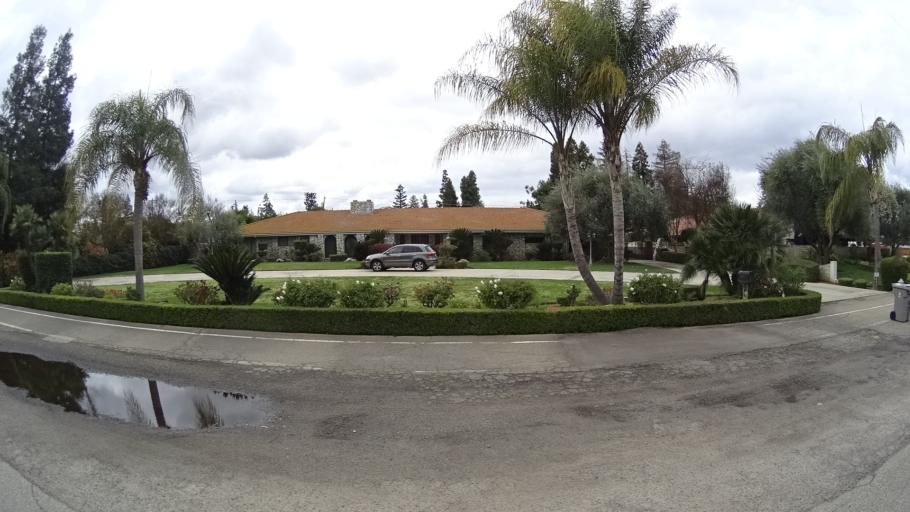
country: US
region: California
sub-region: Fresno County
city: Fresno
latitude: 36.8141
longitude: -119.8355
